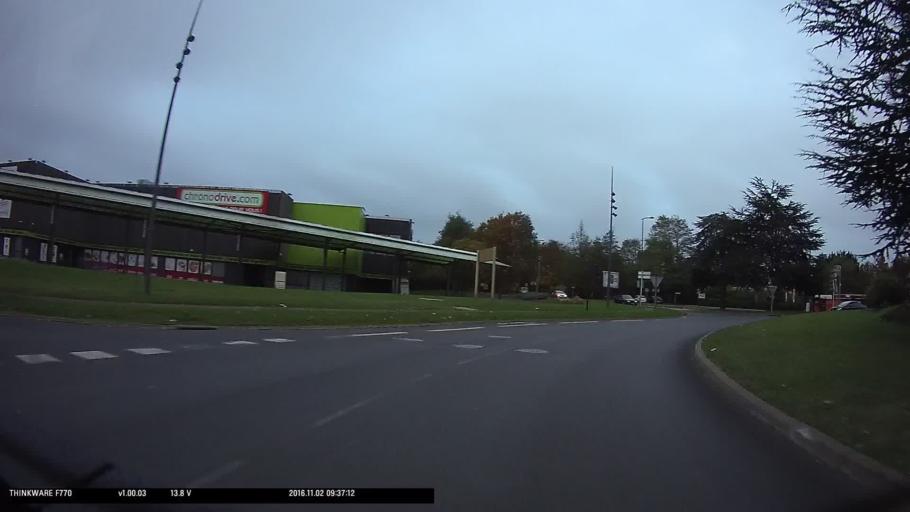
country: FR
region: Ile-de-France
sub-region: Departement du Val-d'Oise
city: Vaureal
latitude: 49.0542
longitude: 2.0246
